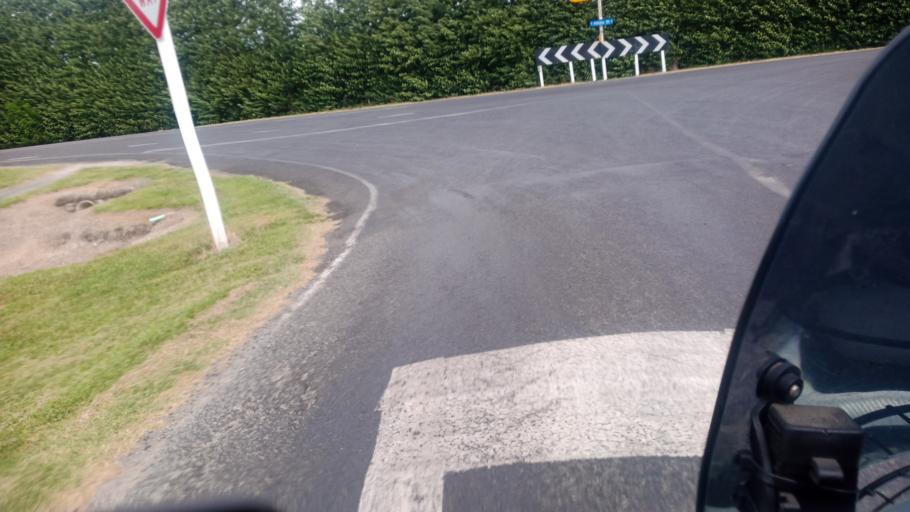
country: NZ
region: Gisborne
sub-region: Gisborne District
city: Gisborne
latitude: -38.6257
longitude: 177.8894
